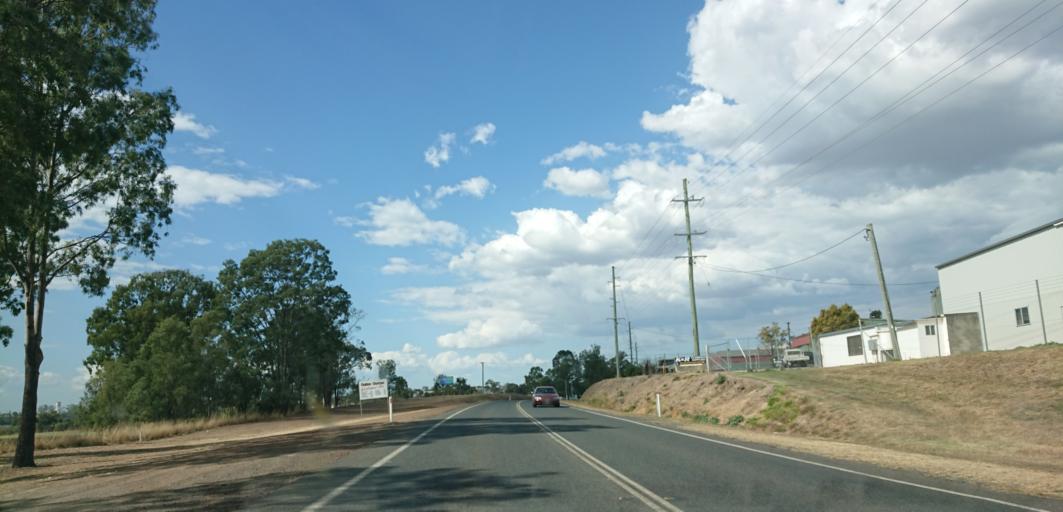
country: AU
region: Queensland
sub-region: Lockyer Valley
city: Gatton
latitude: -27.5720
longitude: 152.2583
